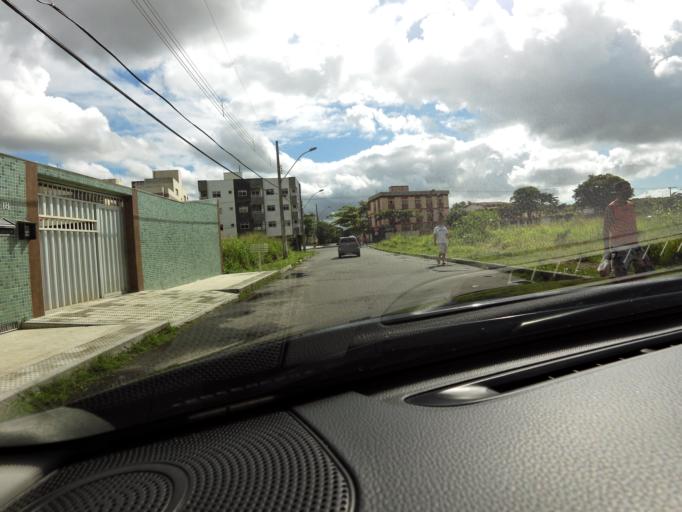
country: BR
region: Espirito Santo
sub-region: Guarapari
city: Guarapari
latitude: -20.6512
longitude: -40.4772
